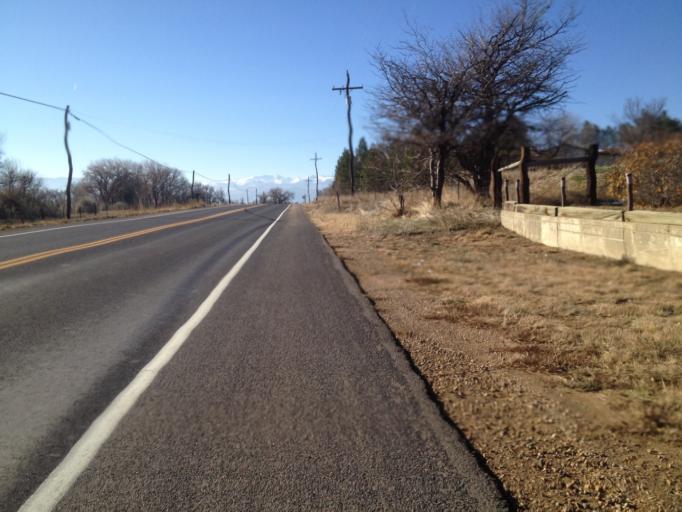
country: US
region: Colorado
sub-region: Boulder County
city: Gunbarrel
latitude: 40.0401
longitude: -105.1357
